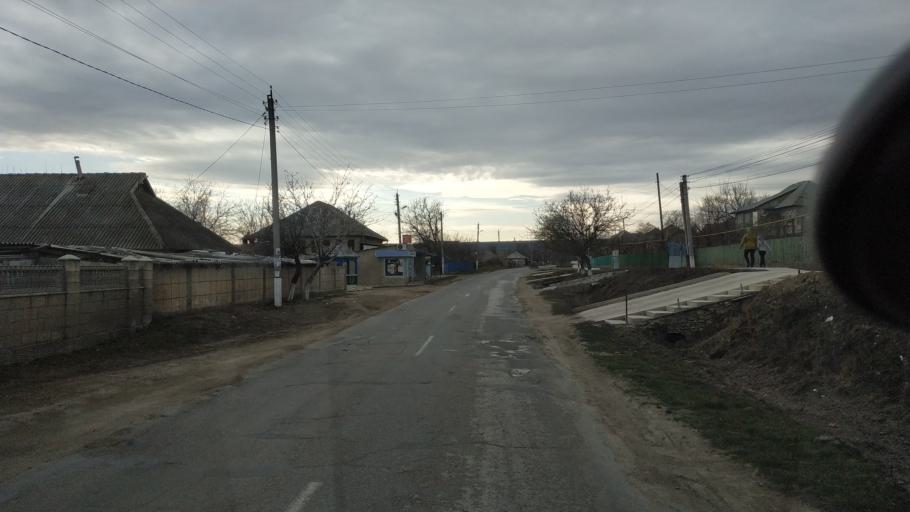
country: MD
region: Chisinau
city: Vadul lui Voda
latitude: 47.1461
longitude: 29.0757
